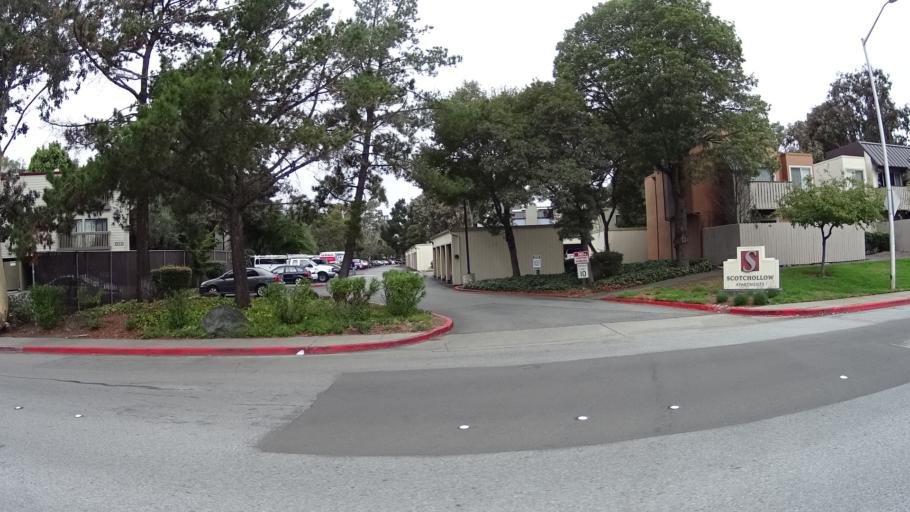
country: US
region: California
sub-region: San Mateo County
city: Belmont
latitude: 37.5318
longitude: -122.2853
